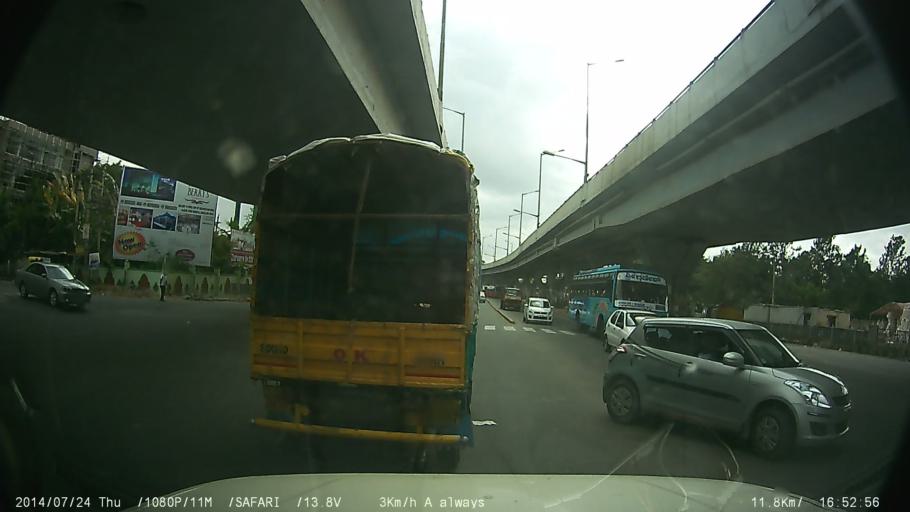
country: IN
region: Karnataka
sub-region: Bangalore Urban
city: Bangalore
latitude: 12.9242
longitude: 77.6518
